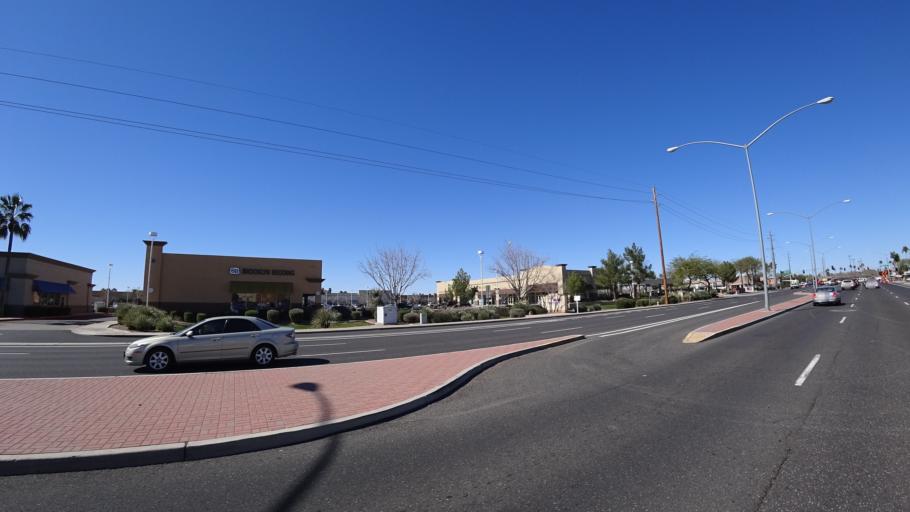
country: US
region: Arizona
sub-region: Maricopa County
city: Gilbert
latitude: 33.3776
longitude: -111.6878
